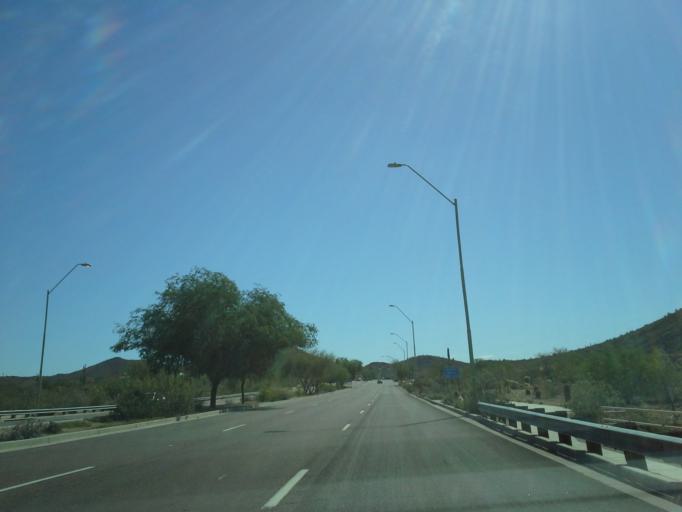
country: US
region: Arizona
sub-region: Maricopa County
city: Fountain Hills
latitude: 33.5823
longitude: -111.7944
